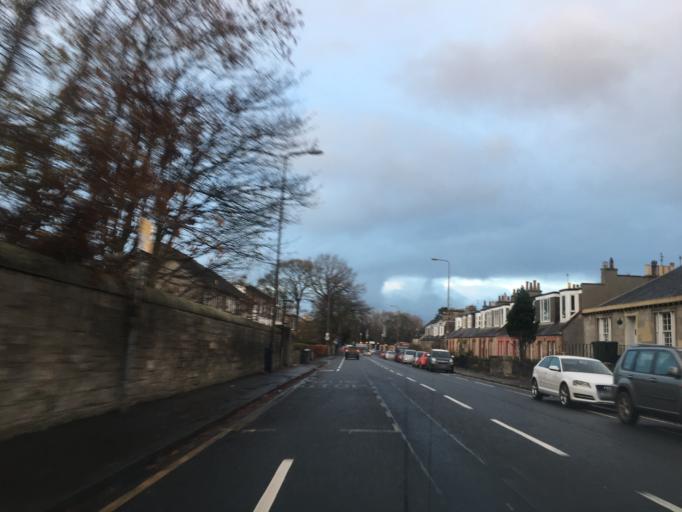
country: GB
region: Scotland
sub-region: Edinburgh
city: Colinton
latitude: 55.9637
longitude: -3.2737
